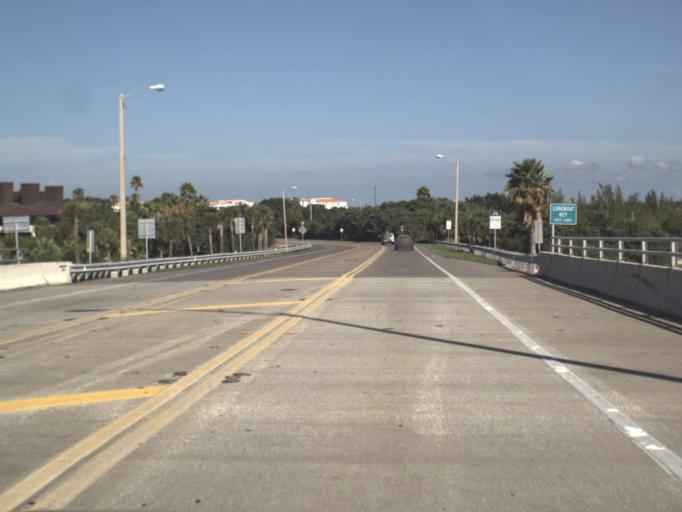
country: US
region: Florida
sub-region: Sarasota County
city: Siesta Key
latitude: 27.3341
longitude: -82.5826
